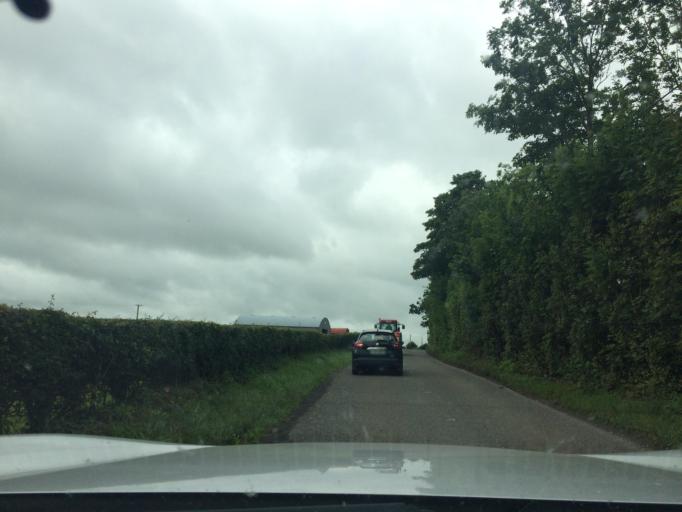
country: IE
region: Munster
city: Thurles
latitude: 52.6271
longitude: -7.8743
